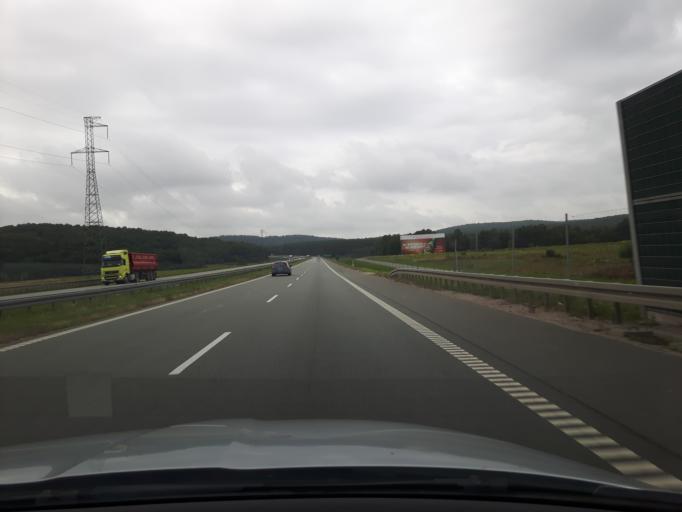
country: PL
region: Swietokrzyskie
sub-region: Powiat kielecki
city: Checiny
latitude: 50.8382
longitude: 20.4782
